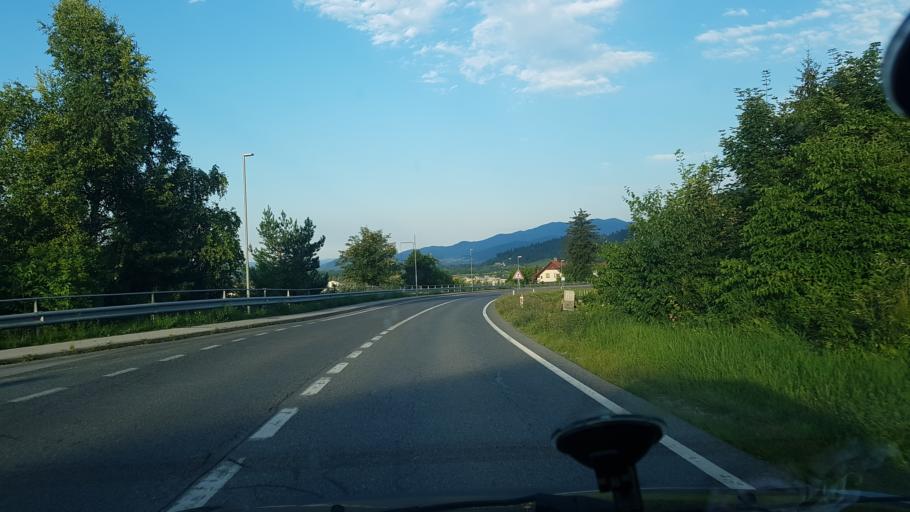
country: SI
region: Vrhnika
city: Vrhnika
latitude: 45.9621
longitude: 14.2842
